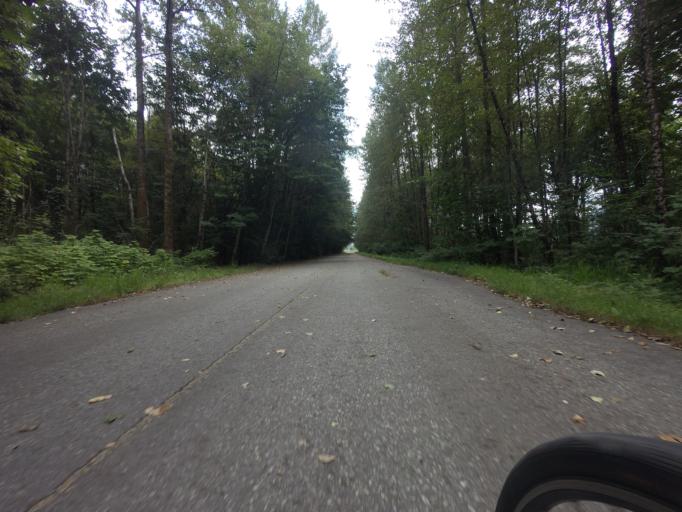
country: CA
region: British Columbia
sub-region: Greater Vancouver Regional District
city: Lions Bay
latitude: 49.7279
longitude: -123.1481
